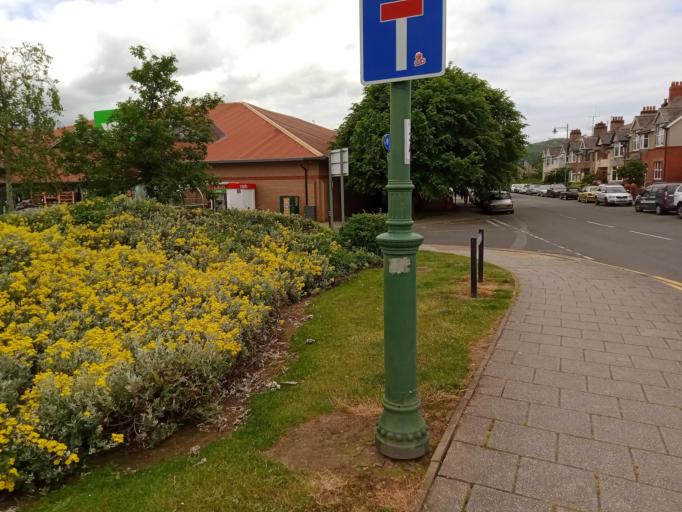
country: GB
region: Wales
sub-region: Conwy
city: Conwy
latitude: 53.2848
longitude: -3.8106
